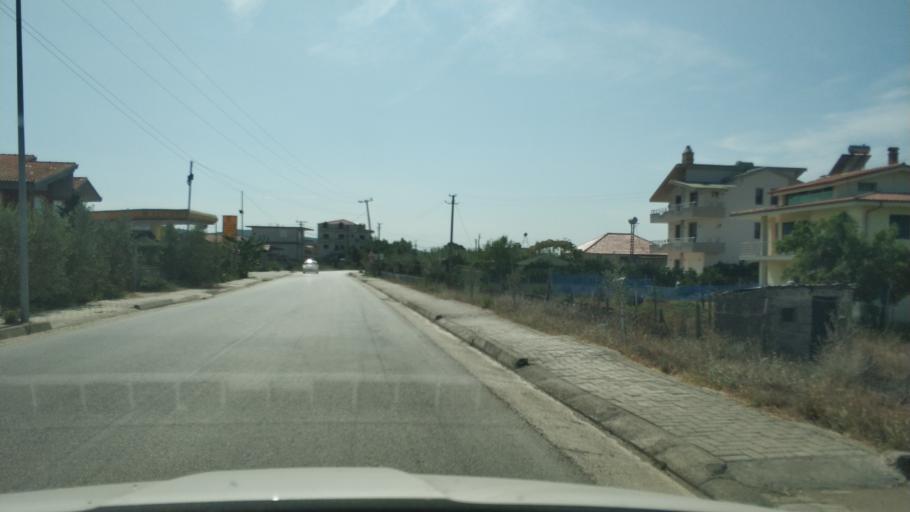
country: AL
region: Fier
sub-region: Rrethi i Lushnjes
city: Divjake
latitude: 40.9789
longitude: 19.5353
